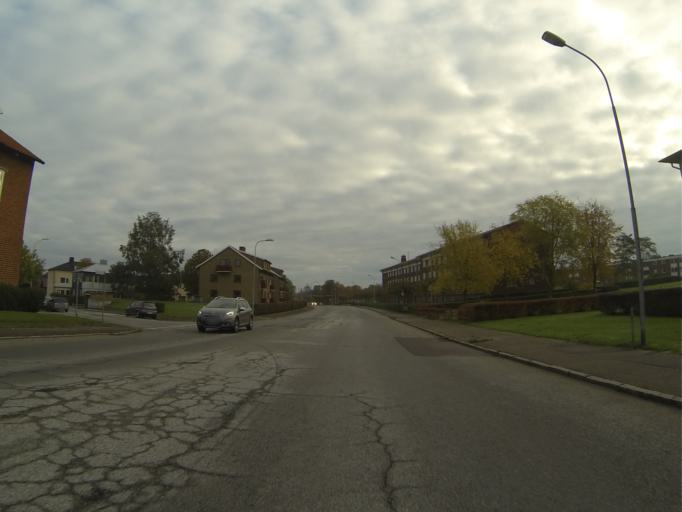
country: SE
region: Skane
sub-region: Tomelilla Kommun
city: Tomelilla
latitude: 55.5412
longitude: 13.9489
